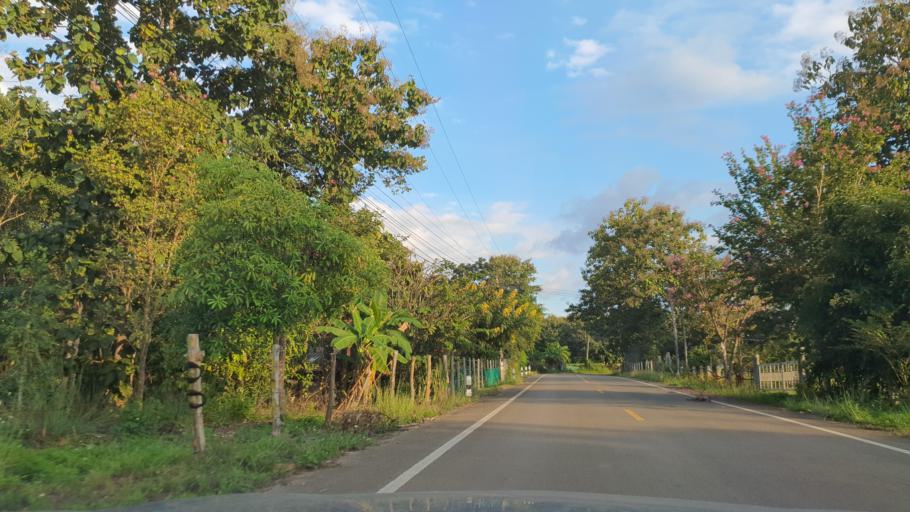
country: TH
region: Chiang Mai
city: Mae On
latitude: 18.8637
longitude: 99.2467
